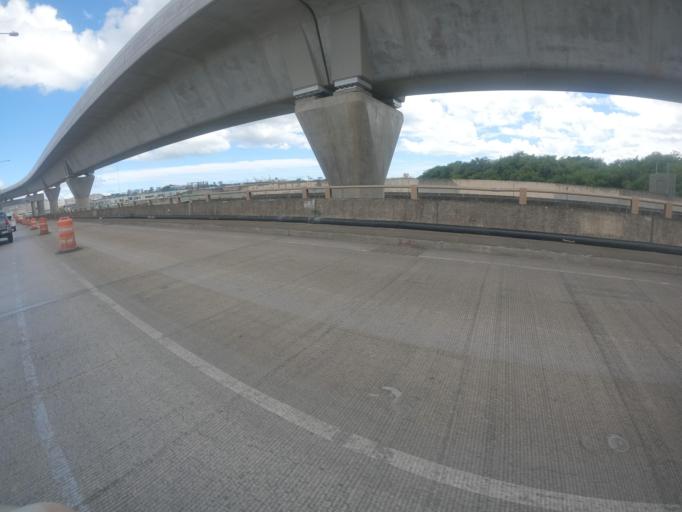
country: US
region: Hawaii
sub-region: Honolulu County
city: Honolulu
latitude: 21.3334
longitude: -157.8935
